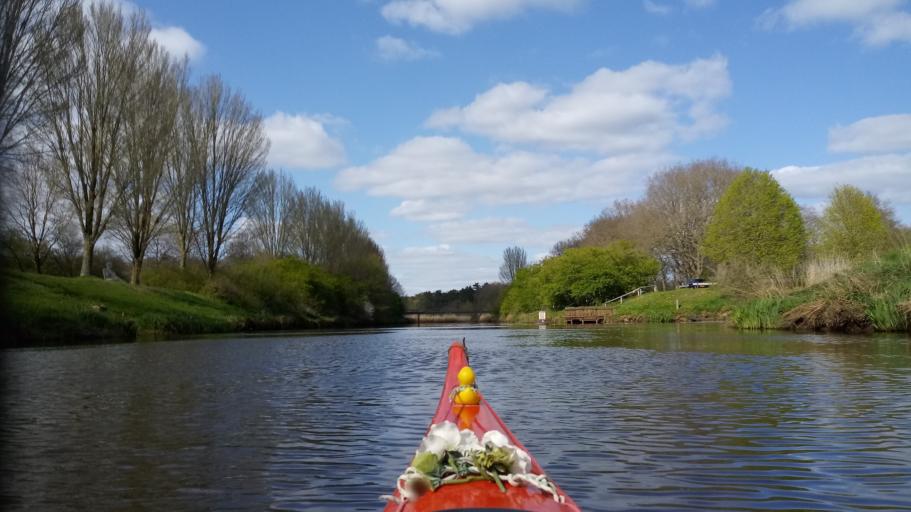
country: NL
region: Overijssel
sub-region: Gemeente Twenterand
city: Den Ham
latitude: 52.4693
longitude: 6.4524
